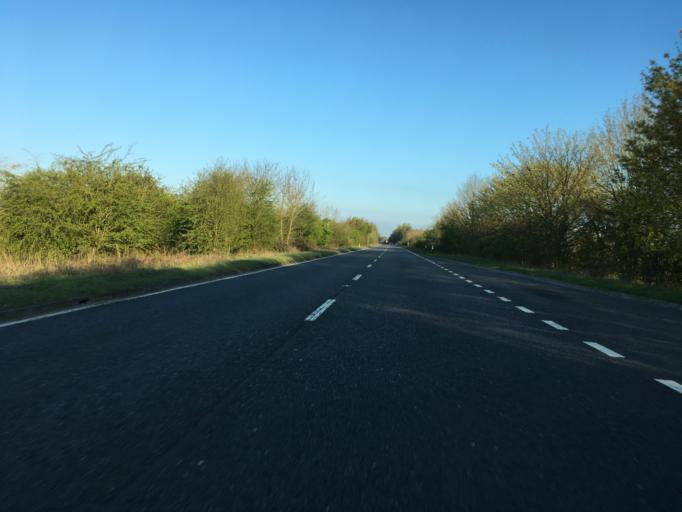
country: GB
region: England
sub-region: Gloucestershire
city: Northleach
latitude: 51.8320
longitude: -1.8201
